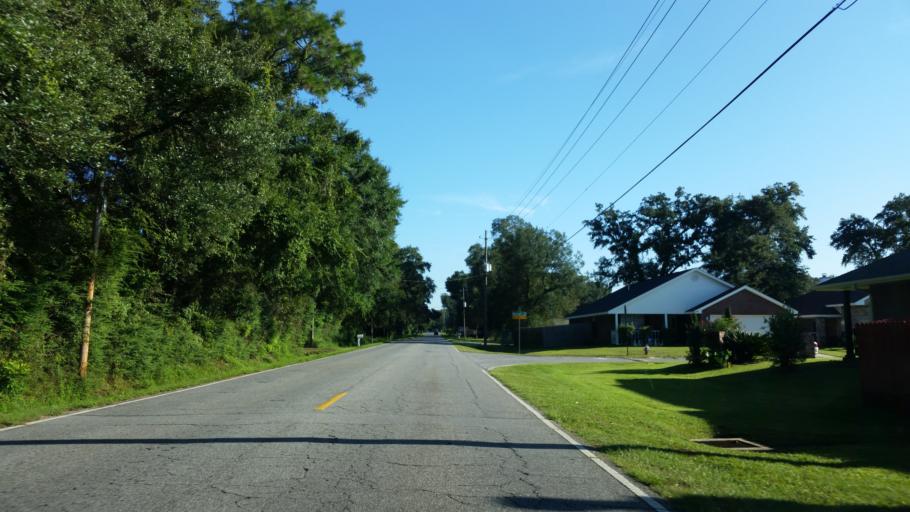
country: US
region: Florida
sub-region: Escambia County
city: Bellview
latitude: 30.4566
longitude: -87.3160
